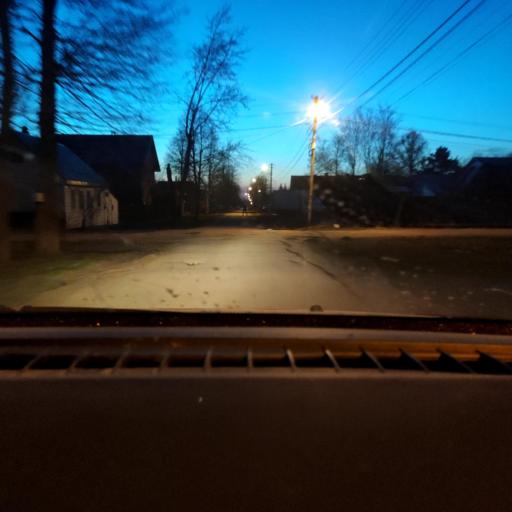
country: RU
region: Perm
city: Perm
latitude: 58.0246
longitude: 56.3255
